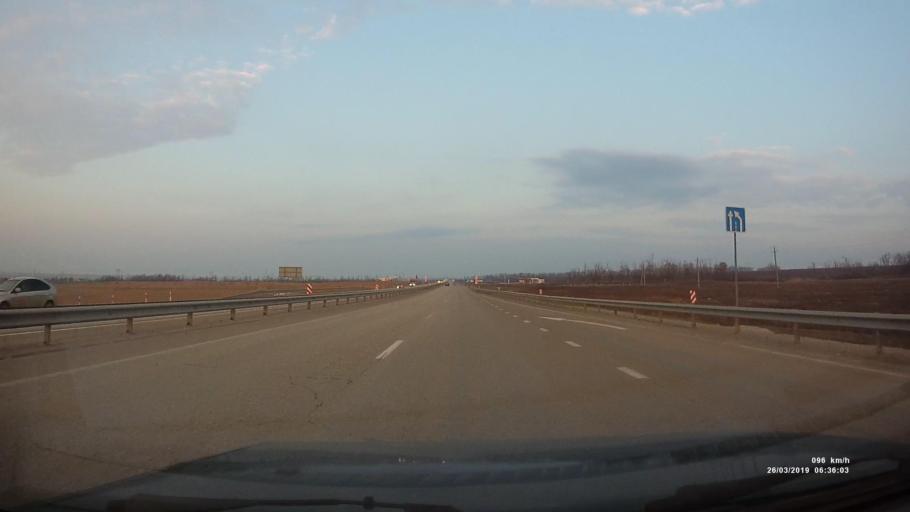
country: RU
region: Rostov
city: Chaltyr
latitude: 47.2839
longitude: 39.4333
